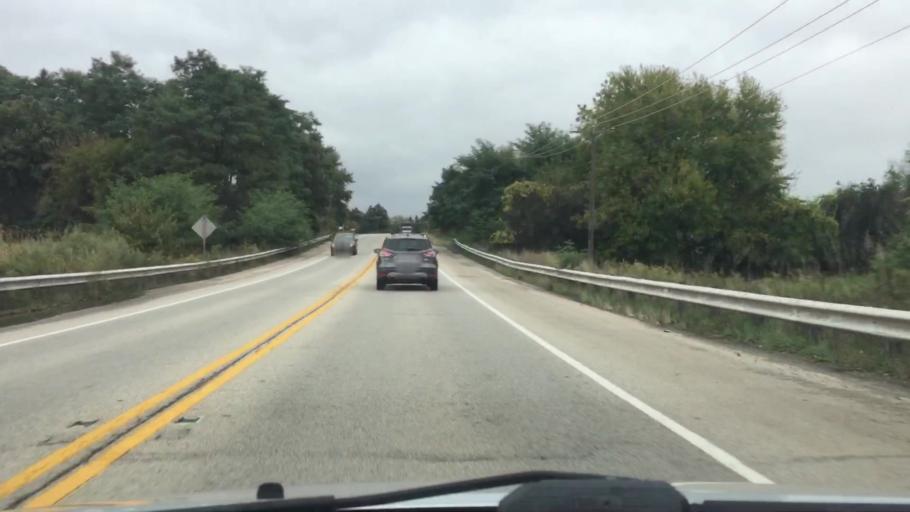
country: US
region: Illinois
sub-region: McHenry County
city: McCullom Lake
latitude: 42.3885
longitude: -88.2855
